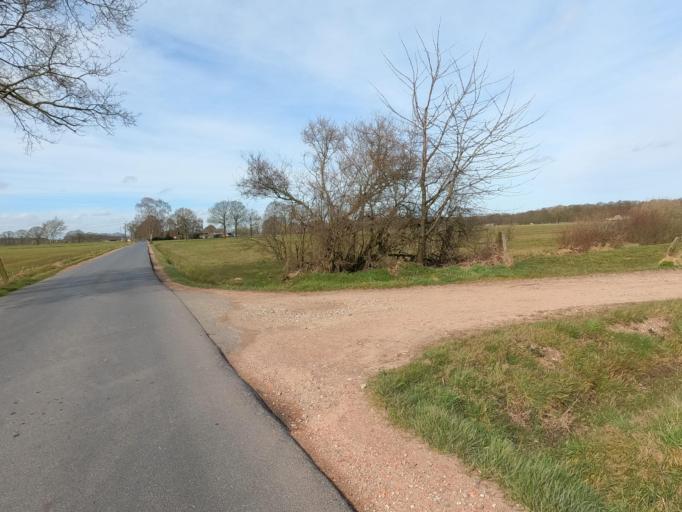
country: BE
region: Flanders
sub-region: Provincie Antwerpen
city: Brecht
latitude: 51.3207
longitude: 4.6558
